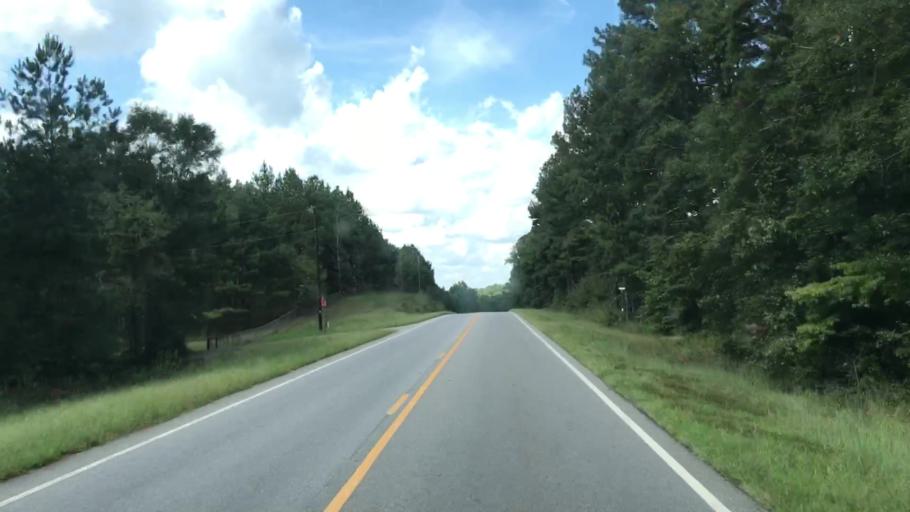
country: US
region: Georgia
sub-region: Greene County
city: Greensboro
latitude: 33.7041
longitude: -83.2862
